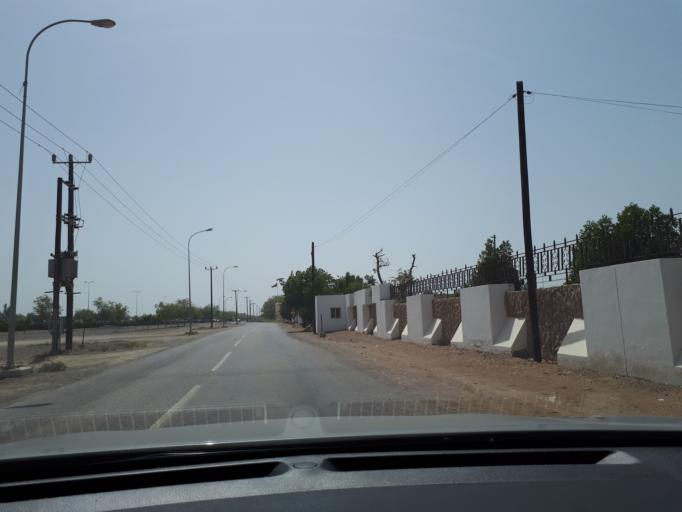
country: OM
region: Muhafazat Masqat
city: As Sib al Jadidah
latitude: 23.6930
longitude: 58.0524
